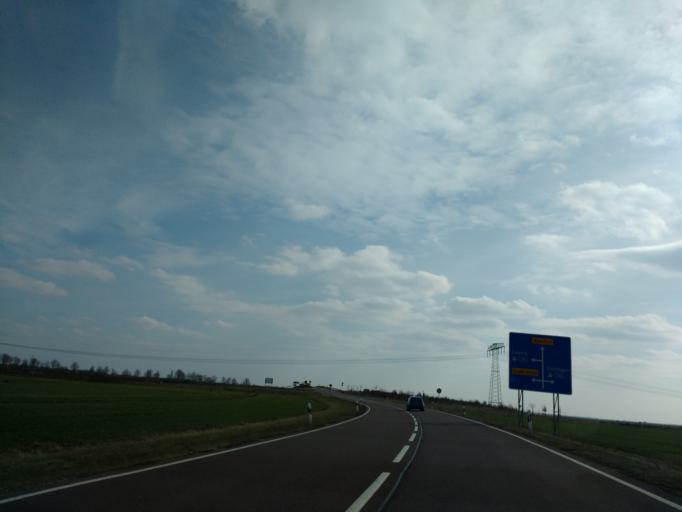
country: DE
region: Saxony-Anhalt
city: Schraplau
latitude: 51.4221
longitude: 11.6483
